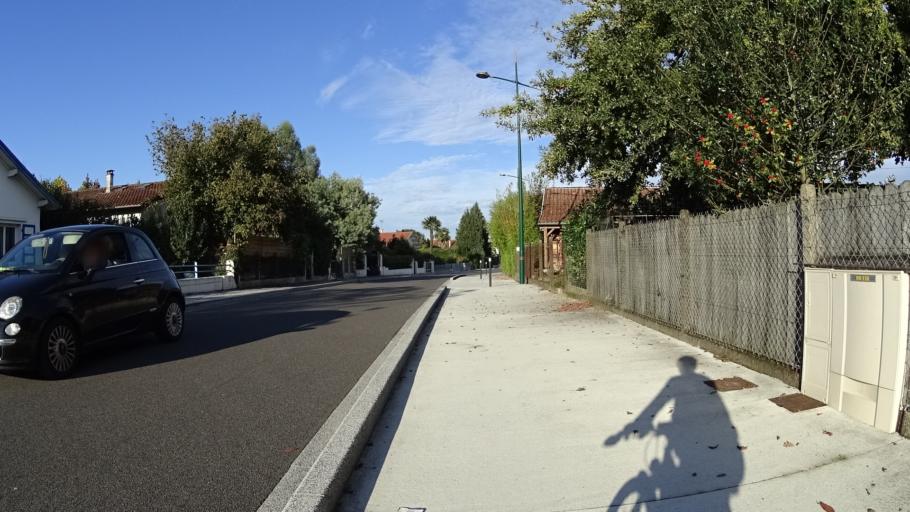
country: FR
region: Aquitaine
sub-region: Departement des Landes
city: Saint-Paul-les-Dax
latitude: 43.7301
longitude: -1.0582
